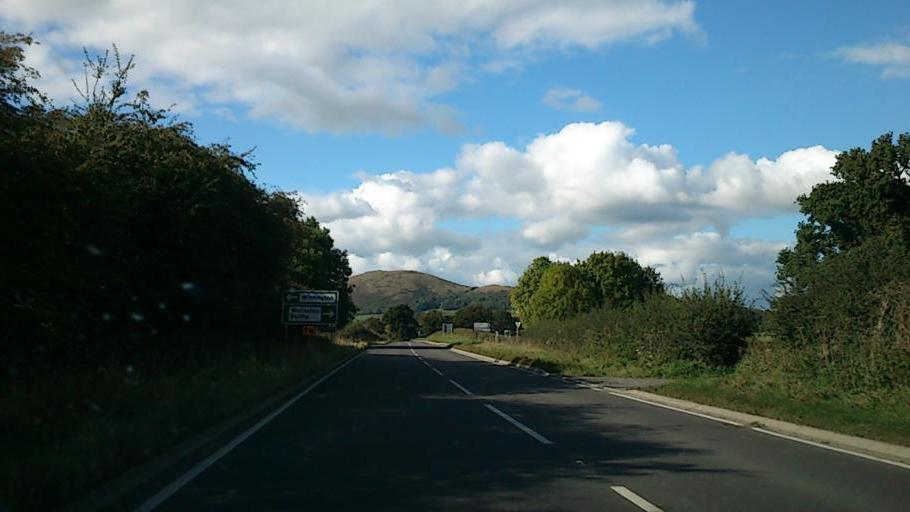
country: GB
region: England
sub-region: Shropshire
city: Westbury
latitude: 52.7005
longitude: -2.9917
